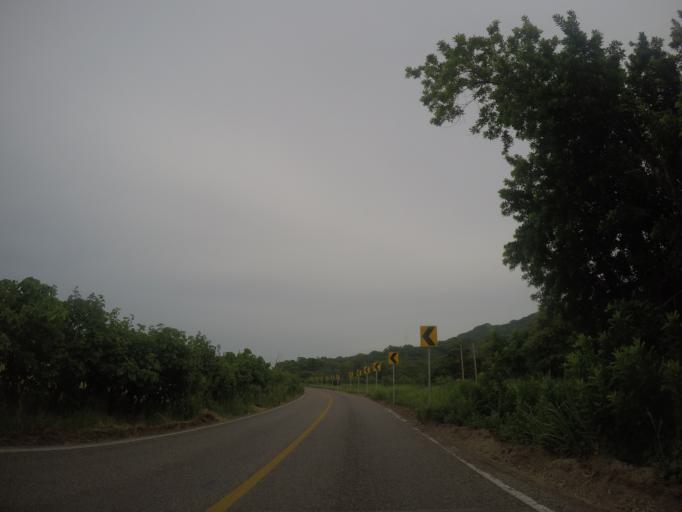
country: MX
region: Oaxaca
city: San Pedro Mixtepec
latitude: 15.9548
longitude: -97.2008
